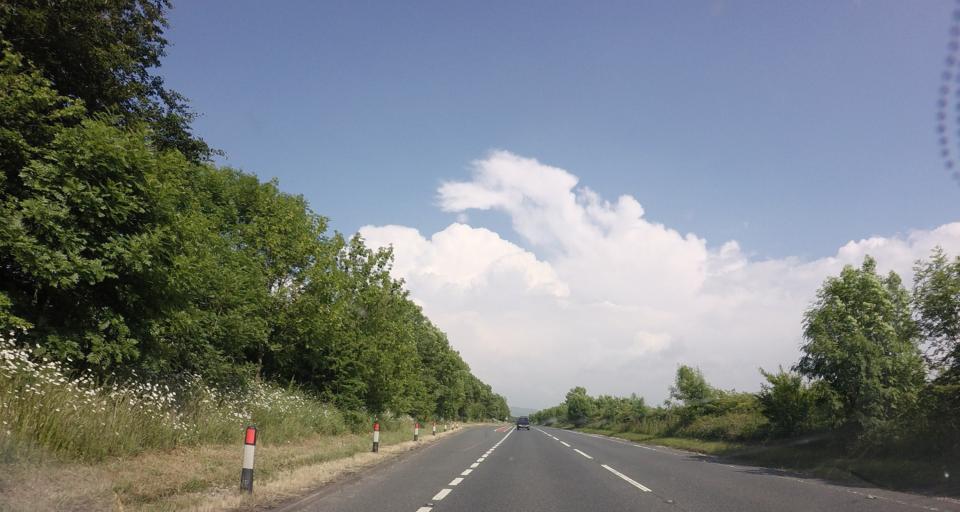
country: GB
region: England
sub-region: Cumbria
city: Cockermouth
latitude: 54.6505
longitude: -3.3555
